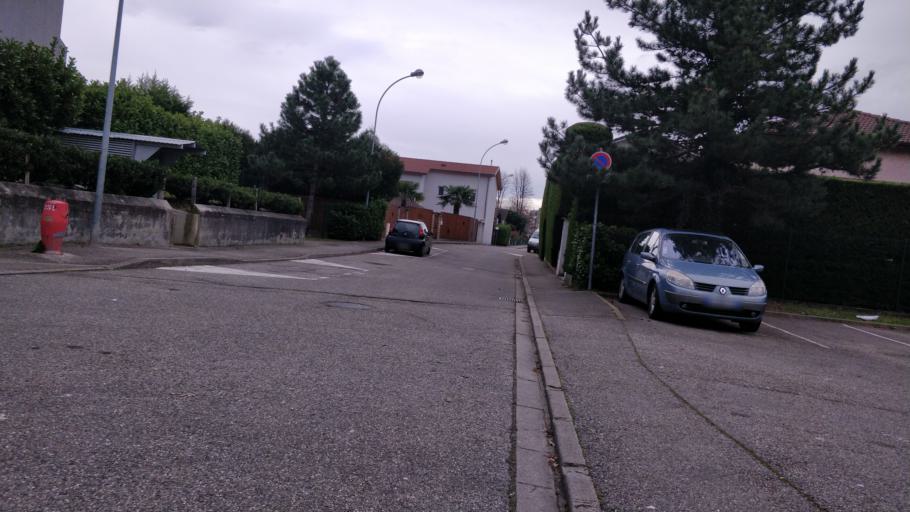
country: FR
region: Rhone-Alpes
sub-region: Departement de l'Isere
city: Fontaine
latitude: 45.1988
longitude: 5.6890
